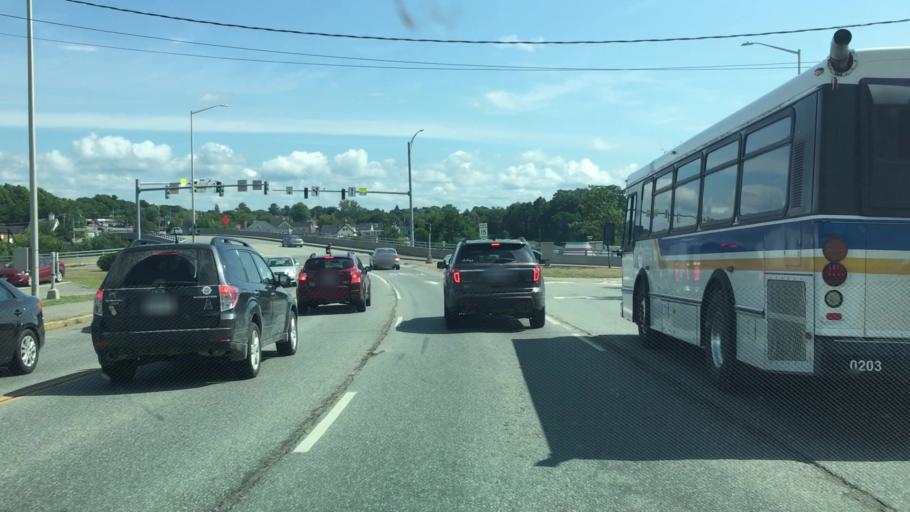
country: US
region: Maine
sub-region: Penobscot County
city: Brewer
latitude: 44.8005
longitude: -68.7663
